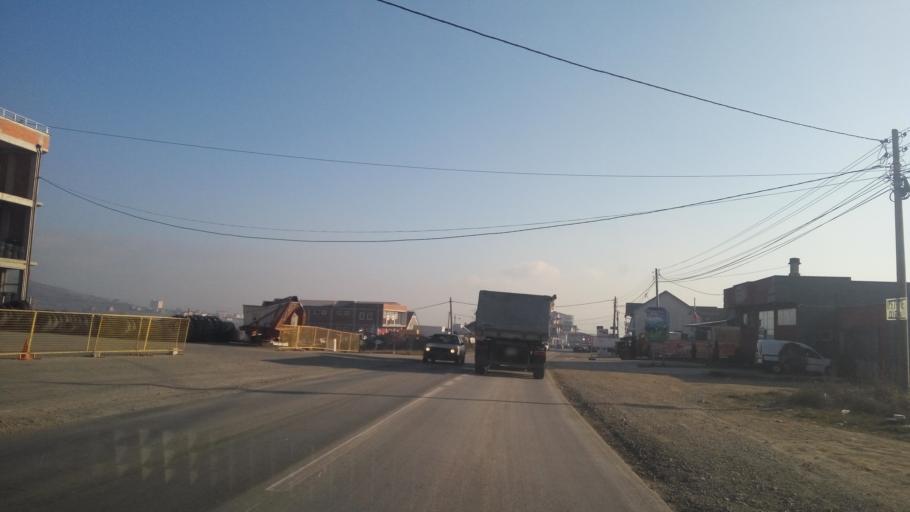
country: XK
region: Gjilan
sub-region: Komuna e Gjilanit
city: Gjilan
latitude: 42.4692
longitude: 21.4348
